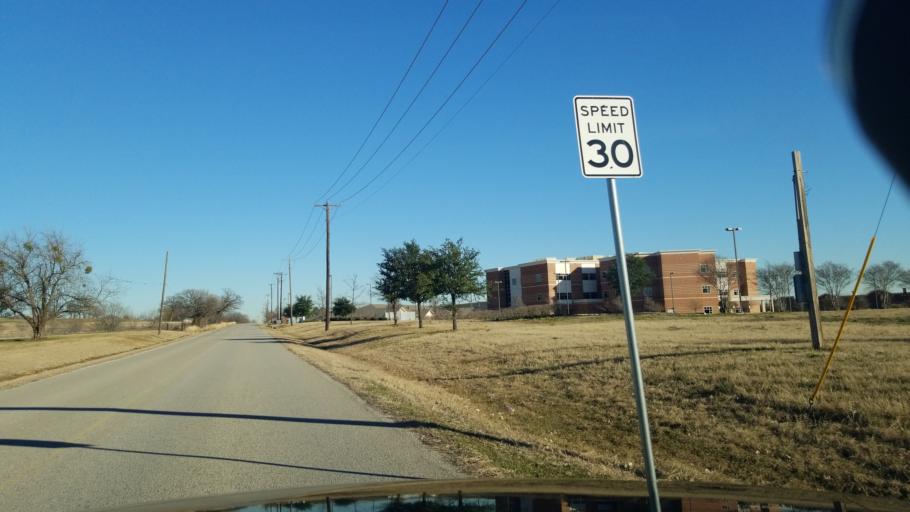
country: US
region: Texas
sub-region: Denton County
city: Corinth
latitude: 33.1545
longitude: -97.0585
